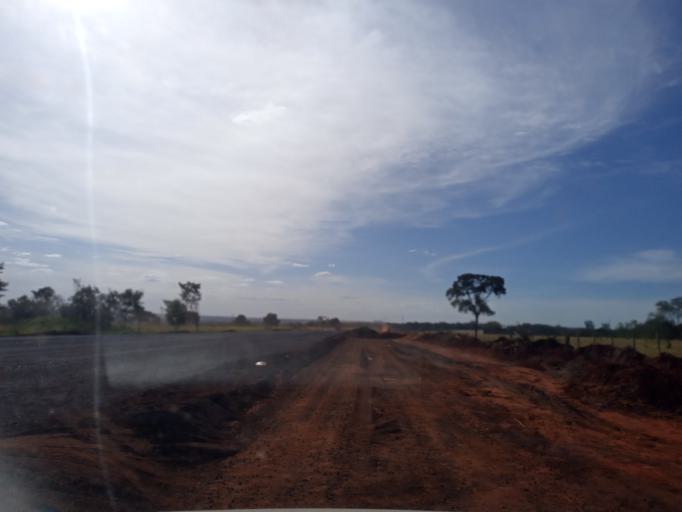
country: BR
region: Minas Gerais
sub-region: Ituiutaba
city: Ituiutaba
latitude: -18.9723
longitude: -49.5053
